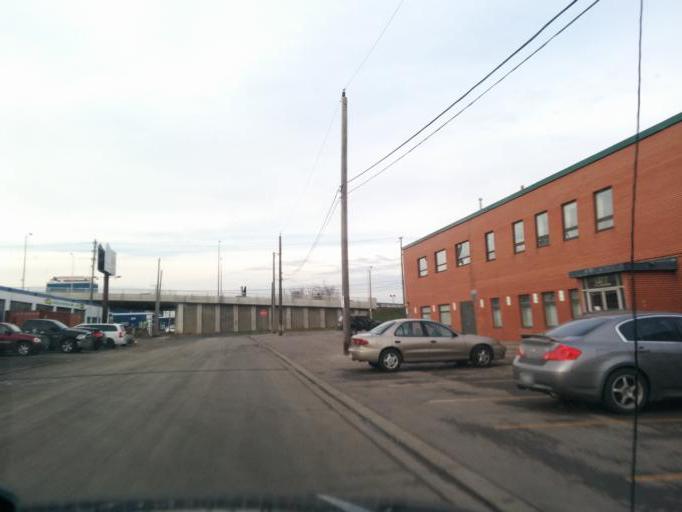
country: CA
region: Ontario
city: Etobicoke
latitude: 43.6192
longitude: -79.5298
